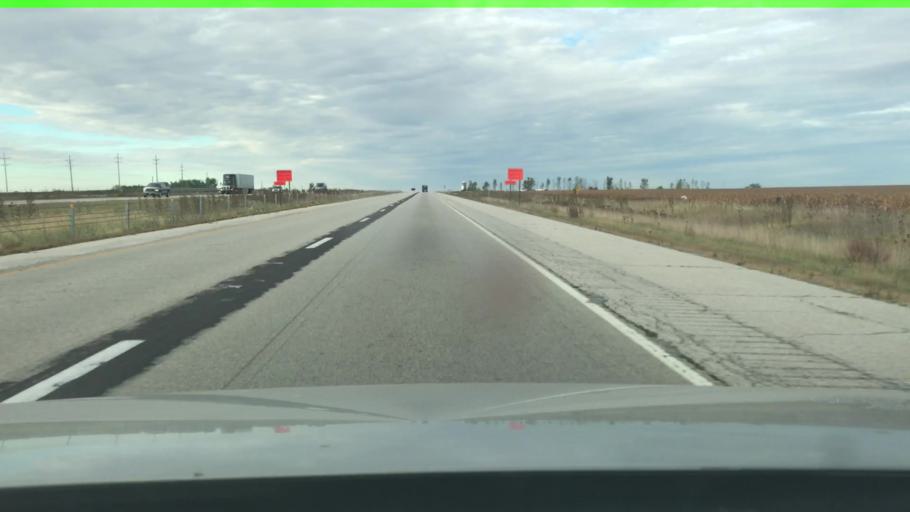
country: US
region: Illinois
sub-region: Livingston County
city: Odell
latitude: 40.9802
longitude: -88.5479
